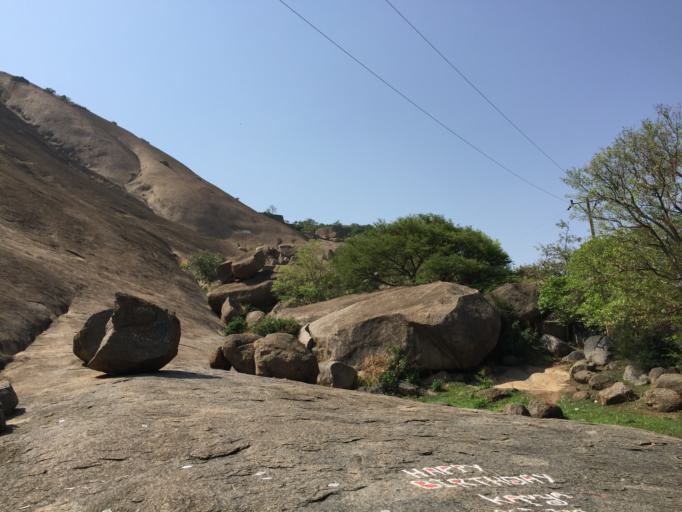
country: IN
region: Karnataka
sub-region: Ramanagara
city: Magadi
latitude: 12.9177
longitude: 77.2989
